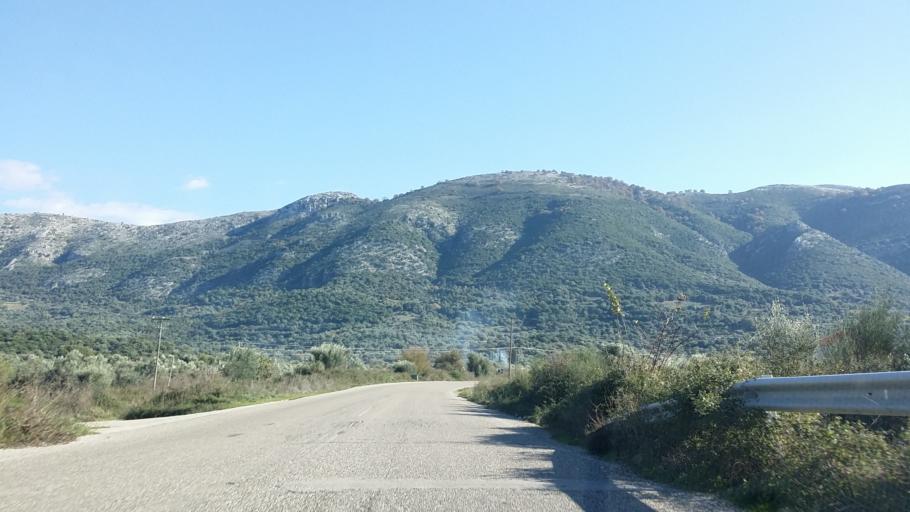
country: GR
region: West Greece
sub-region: Nomos Aitolias kai Akarnanias
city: Kandila
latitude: 38.6759
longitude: 20.9849
